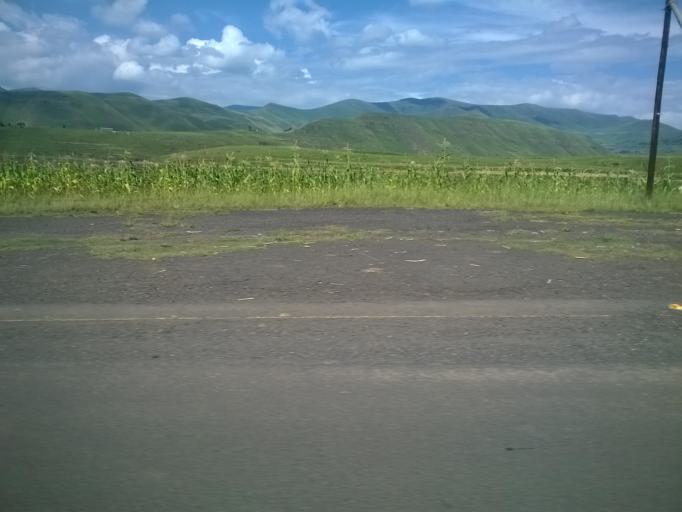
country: LS
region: Thaba-Tseka
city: Thaba-Tseka
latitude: -29.1244
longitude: 28.4918
